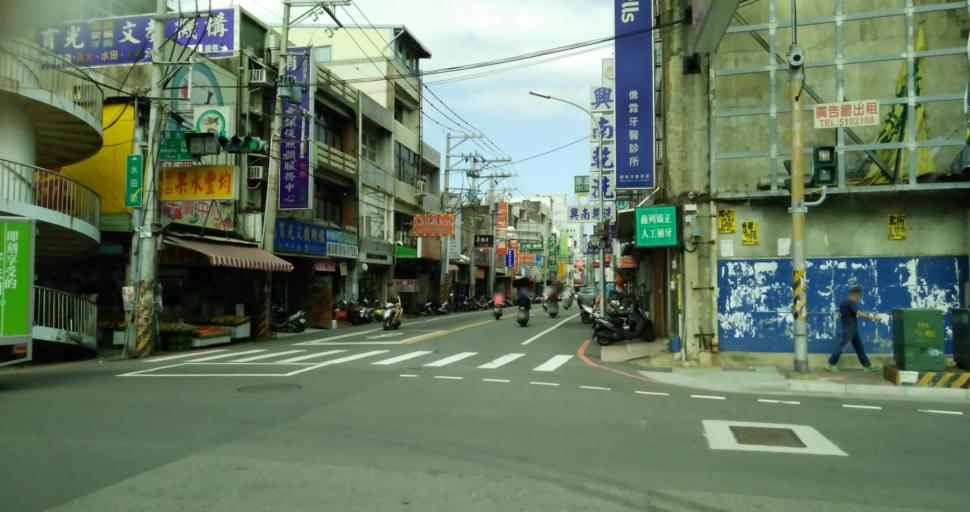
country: TW
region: Taiwan
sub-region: Hsinchu
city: Hsinchu
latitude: 24.8146
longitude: 120.9669
